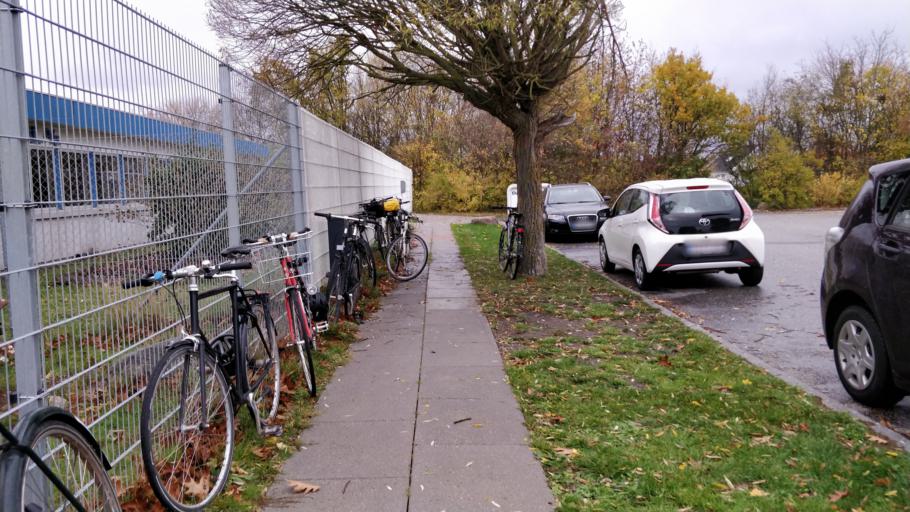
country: DK
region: Capital Region
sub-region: Tarnby Kommune
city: Tarnby
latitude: 55.6177
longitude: 12.6218
